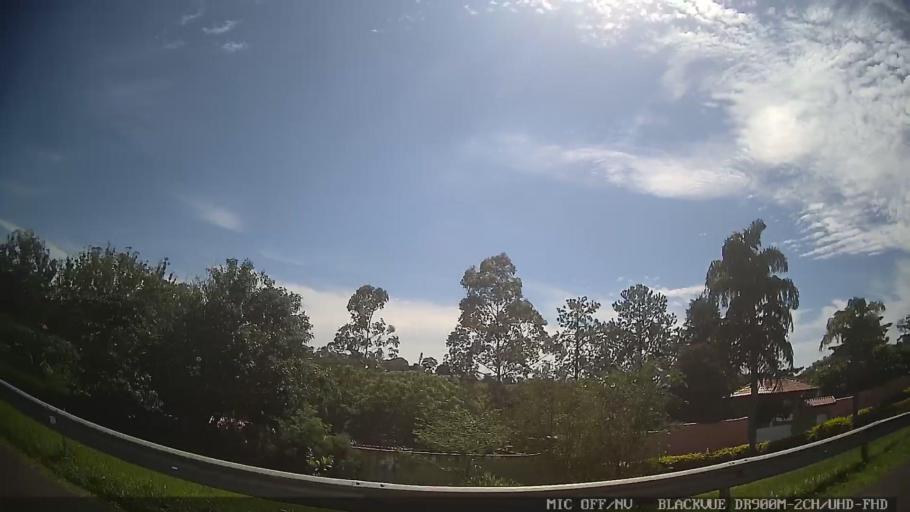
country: BR
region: Sao Paulo
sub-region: Tiete
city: Tiete
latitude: -23.1652
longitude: -47.6461
